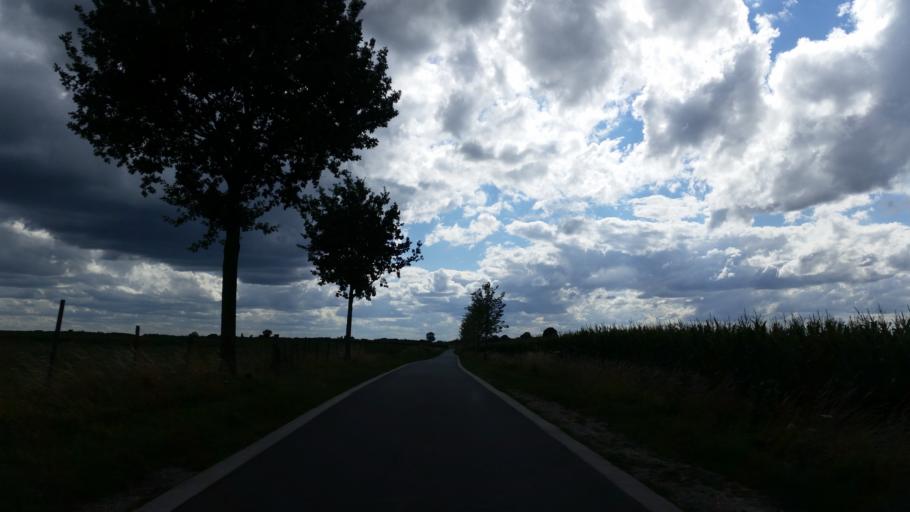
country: NL
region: Limburg
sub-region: Eijsden-Margraten
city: Margraten
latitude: 50.7834
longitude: 5.8250
